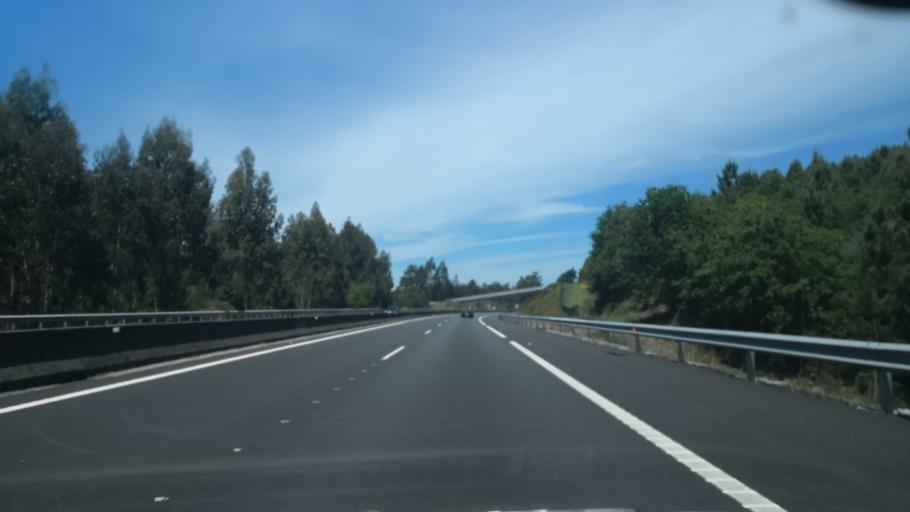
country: ES
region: Galicia
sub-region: Provincia de Pontevedra
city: Valga
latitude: 42.6914
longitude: -8.6342
